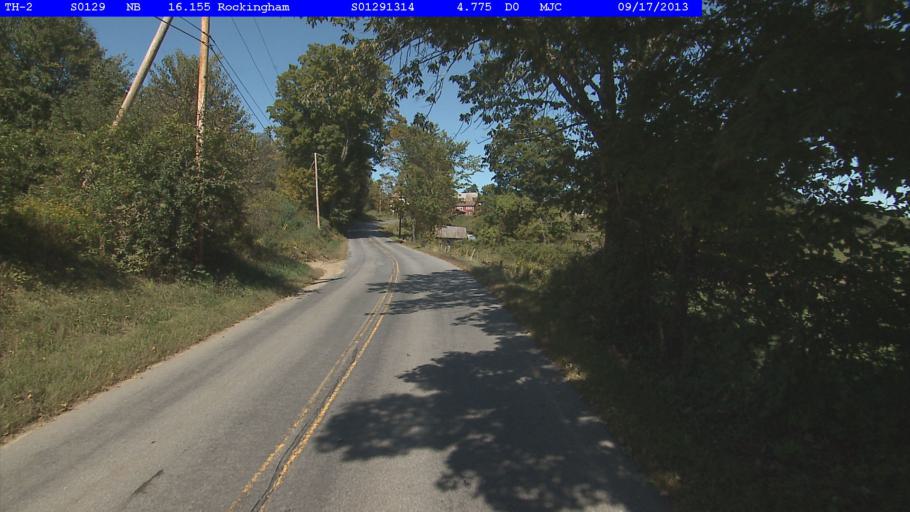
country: US
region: Vermont
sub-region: Windham County
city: Rockingham
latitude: 43.1853
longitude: -72.5127
